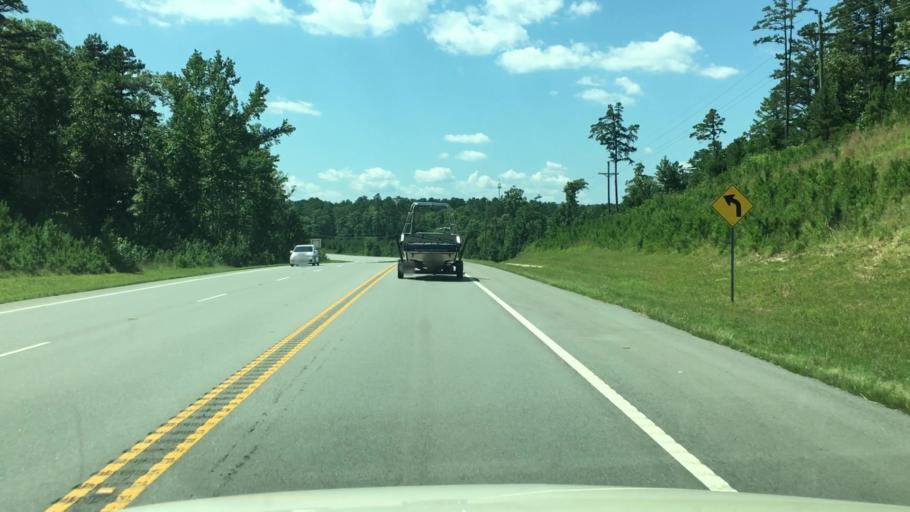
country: US
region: Arkansas
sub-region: Garland County
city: Rockwell
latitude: 34.5202
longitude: -93.3157
